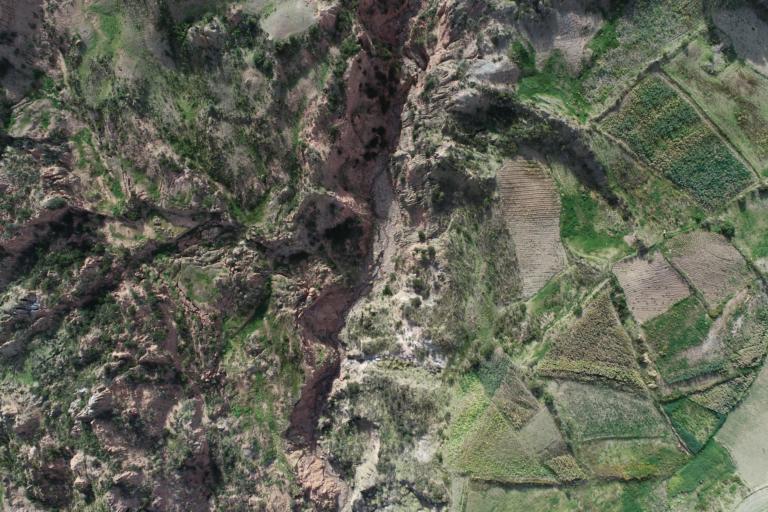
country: BO
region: La Paz
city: La Paz
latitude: -16.5533
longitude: -67.9923
